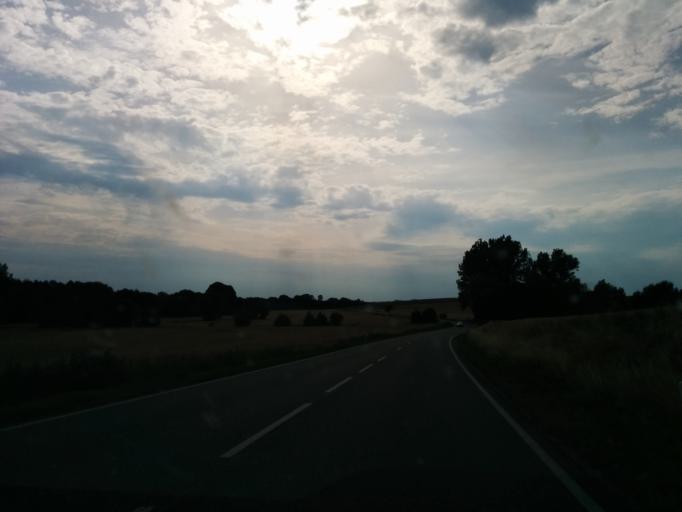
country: DE
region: Thuringia
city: Etzelsrode
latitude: 51.5223
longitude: 10.6561
